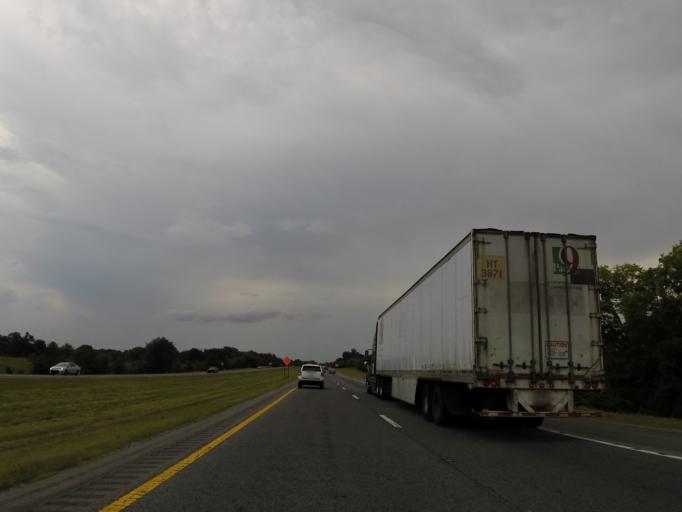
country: US
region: Tennessee
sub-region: Rutherford County
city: Murfreesboro
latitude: 35.9167
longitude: -86.4394
